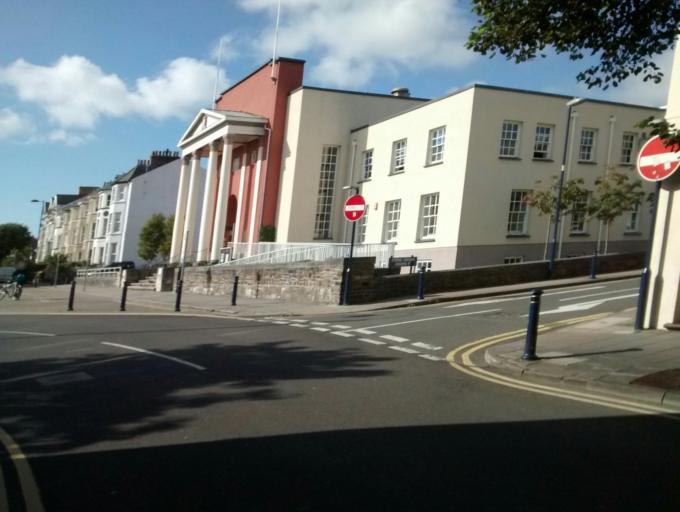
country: GB
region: Wales
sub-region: County of Ceredigion
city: Aberystwyth
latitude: 52.4171
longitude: -4.0815
